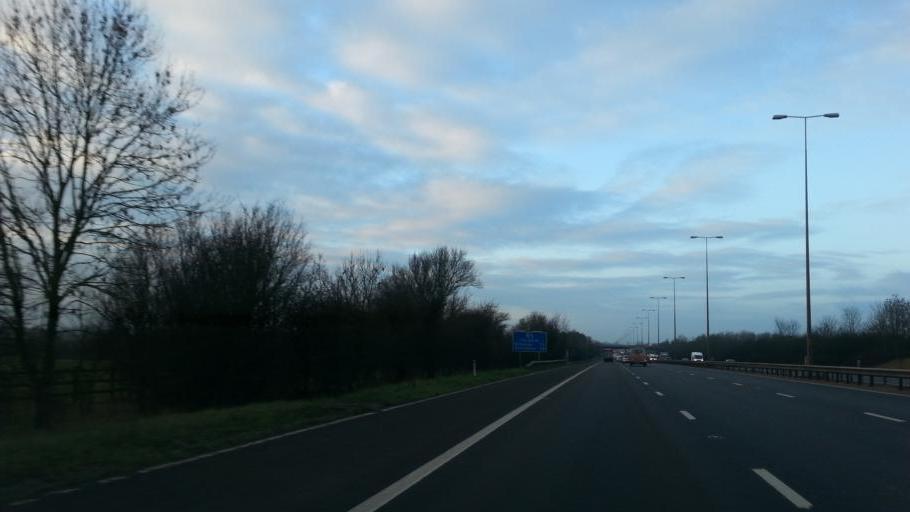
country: GB
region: England
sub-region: Worcestershire
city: Upton upon Severn
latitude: 52.0723
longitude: -2.1629
